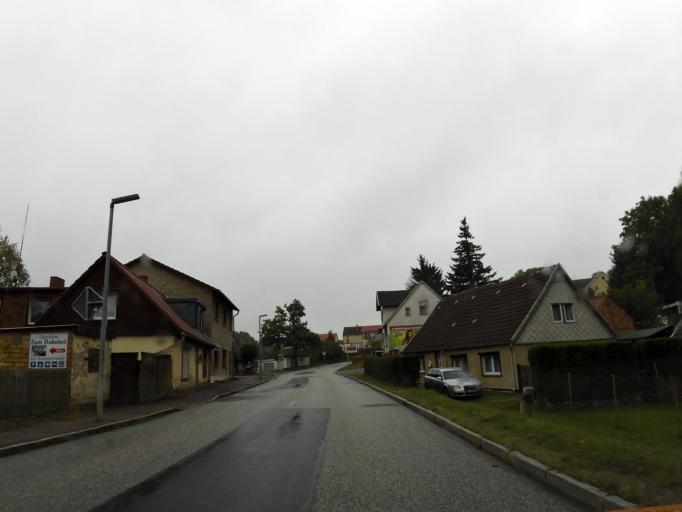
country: DE
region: Saxony-Anhalt
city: Friedrichsbrunn
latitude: 51.6455
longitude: 10.9868
